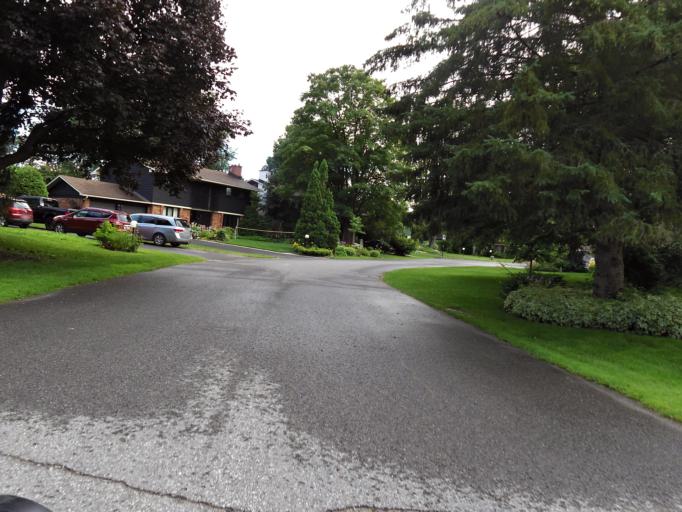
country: CA
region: Ontario
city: Bells Corners
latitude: 45.3340
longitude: -75.9107
